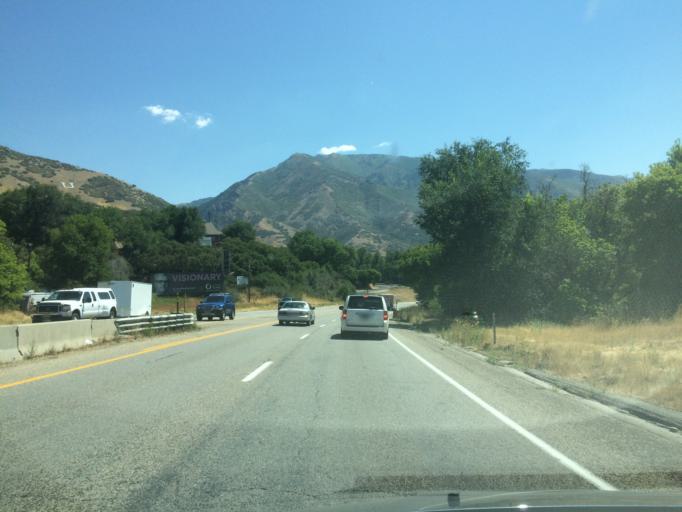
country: US
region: Utah
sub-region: Weber County
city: Uintah
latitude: 41.1463
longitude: -111.9210
